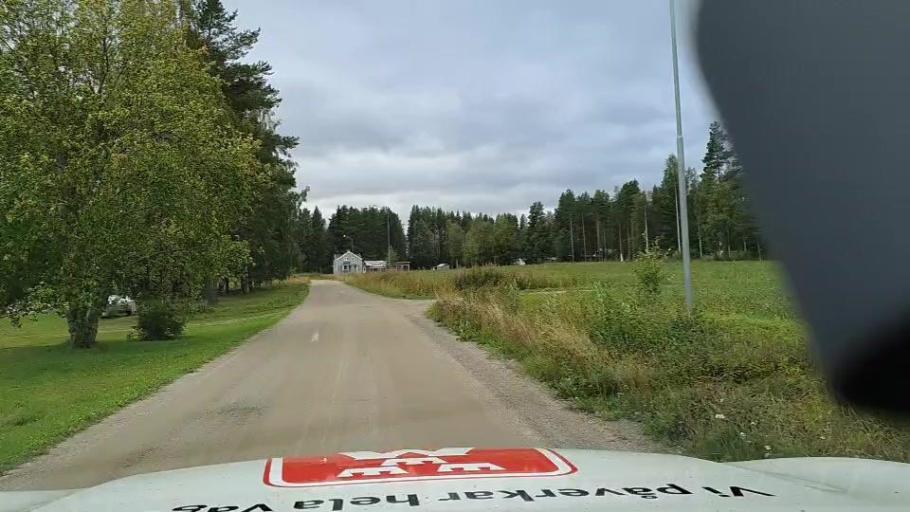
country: SE
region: Jaemtland
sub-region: Ragunda Kommun
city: Hammarstrand
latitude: 63.1712
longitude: 15.8610
